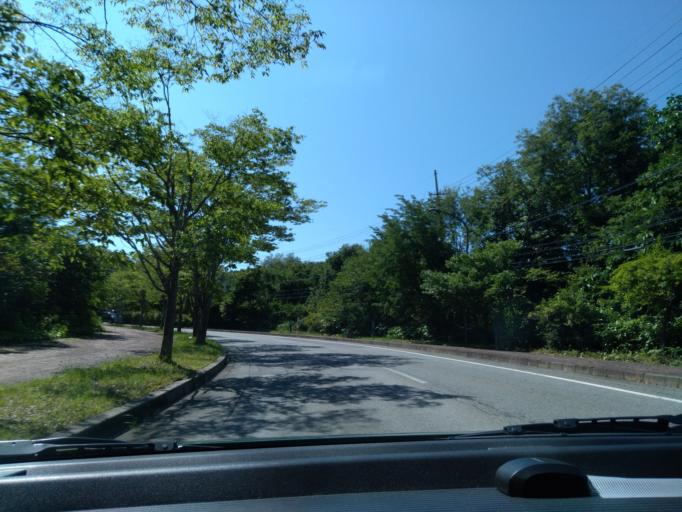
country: JP
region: Akita
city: Kakunodatemachi
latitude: 39.7354
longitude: 140.7035
